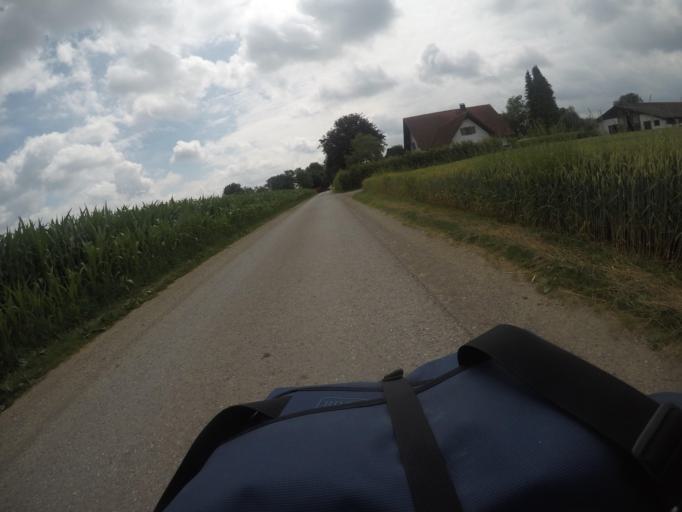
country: DE
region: Bavaria
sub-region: Swabia
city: Fellheim
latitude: 48.0884
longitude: 10.1558
